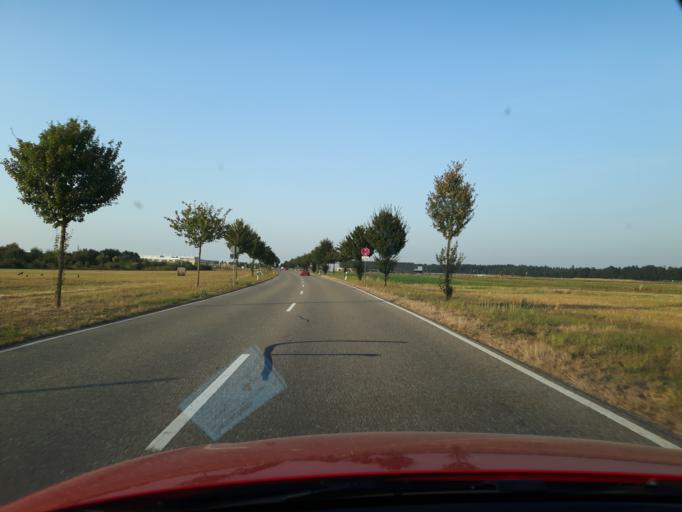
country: DE
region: Baden-Wuerttemberg
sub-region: Karlsruhe Region
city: Rheinstetten
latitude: 48.9700
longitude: 8.3330
